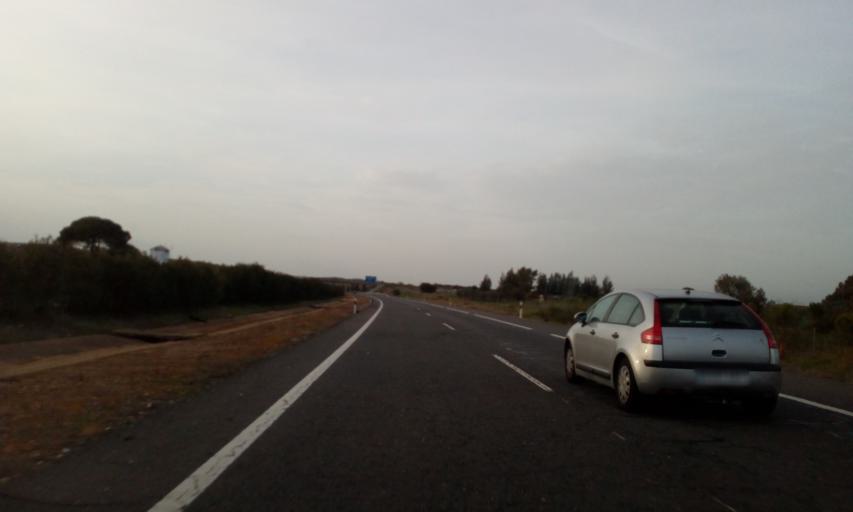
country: ES
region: Andalusia
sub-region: Provincia de Huelva
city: Gibraleon
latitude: 37.3533
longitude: -6.9340
